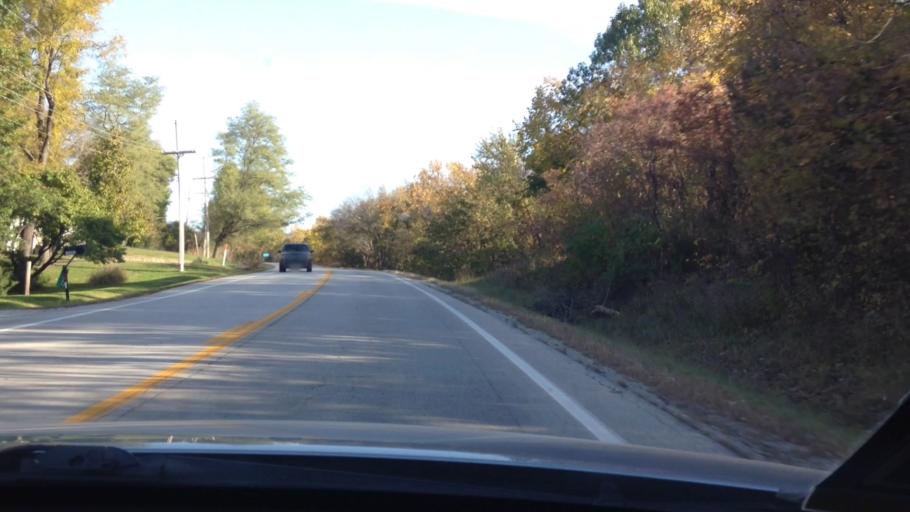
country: US
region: Missouri
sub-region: Platte County
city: Weatherby Lake
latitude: 39.2276
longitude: -94.7762
